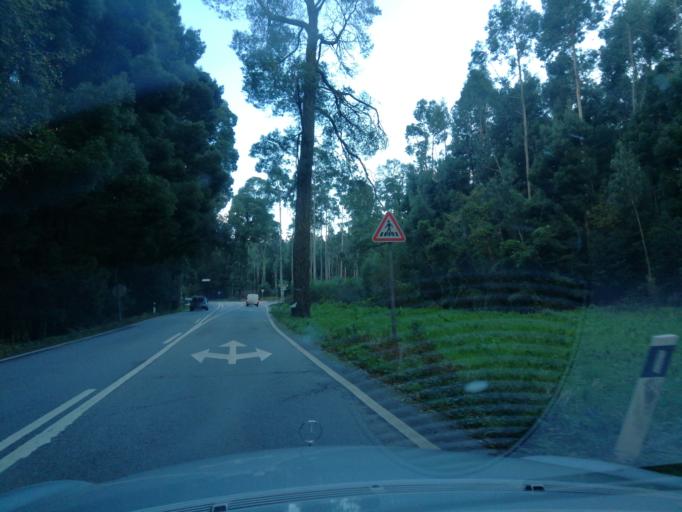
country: PT
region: Braga
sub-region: Esposende
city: Marinhas
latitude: 41.5851
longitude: -8.7342
